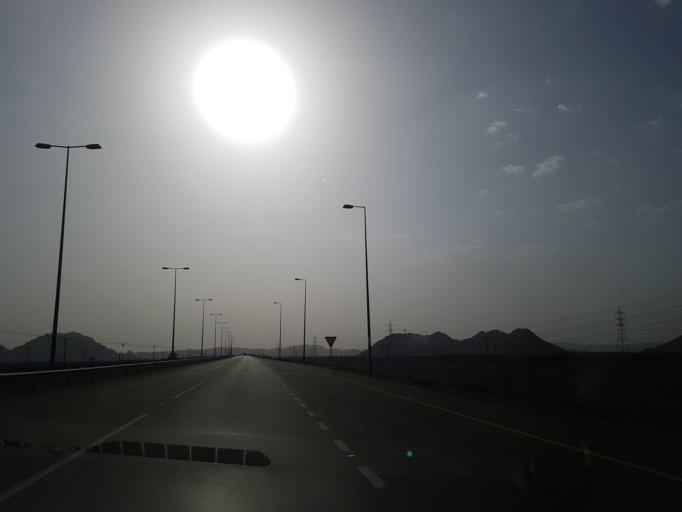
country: OM
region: Al Buraimi
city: Al Buraymi
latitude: 24.2468
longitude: 56.0168
